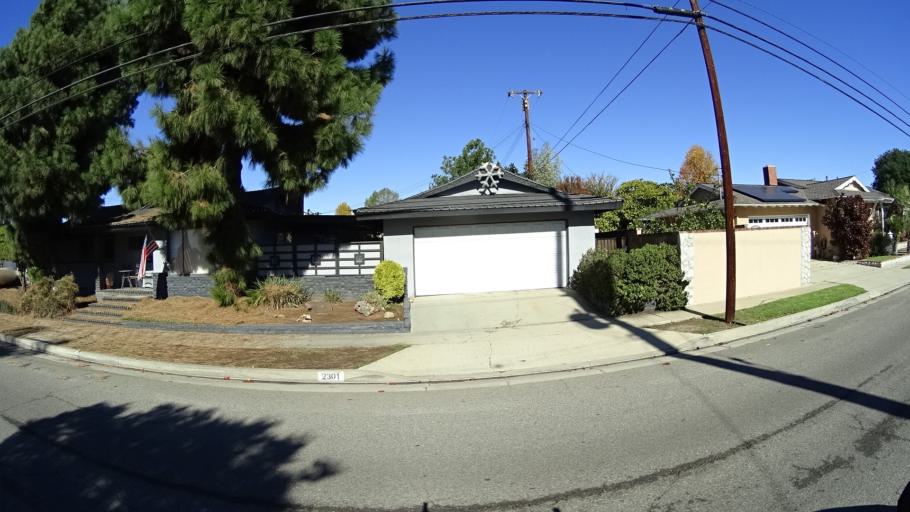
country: US
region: California
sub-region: Orange County
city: La Habra
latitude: 33.9391
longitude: -117.9212
